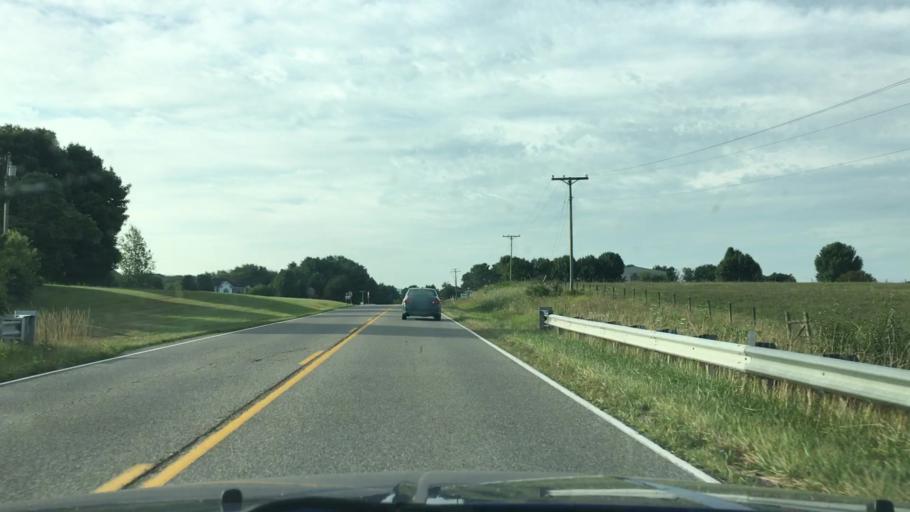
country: US
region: Virginia
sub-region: City of Waynesboro
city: Waynesboro
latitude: 38.1122
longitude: -78.9056
